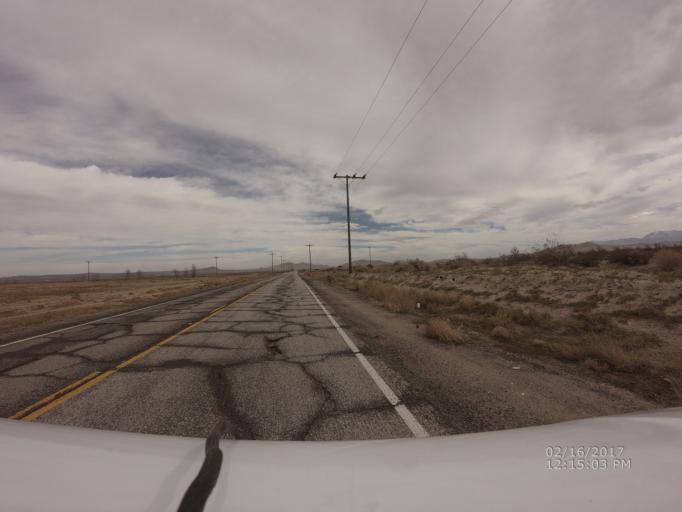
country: US
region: California
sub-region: Los Angeles County
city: Lake Los Angeles
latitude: 34.6754
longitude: -117.9357
